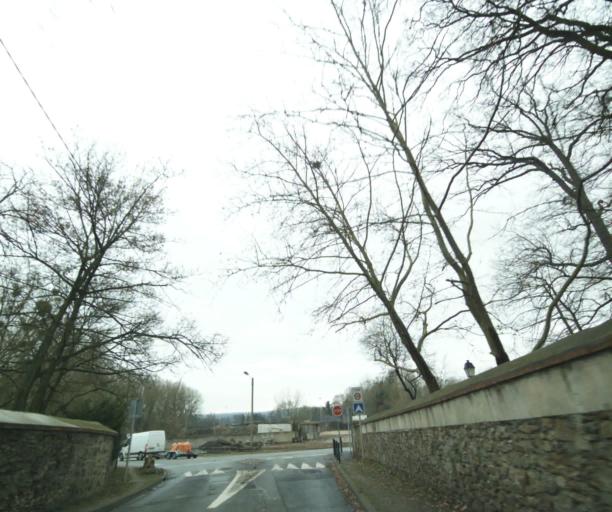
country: FR
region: Ile-de-France
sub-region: Departement de l'Essonne
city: Champlan
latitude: 48.7034
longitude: 2.2709
